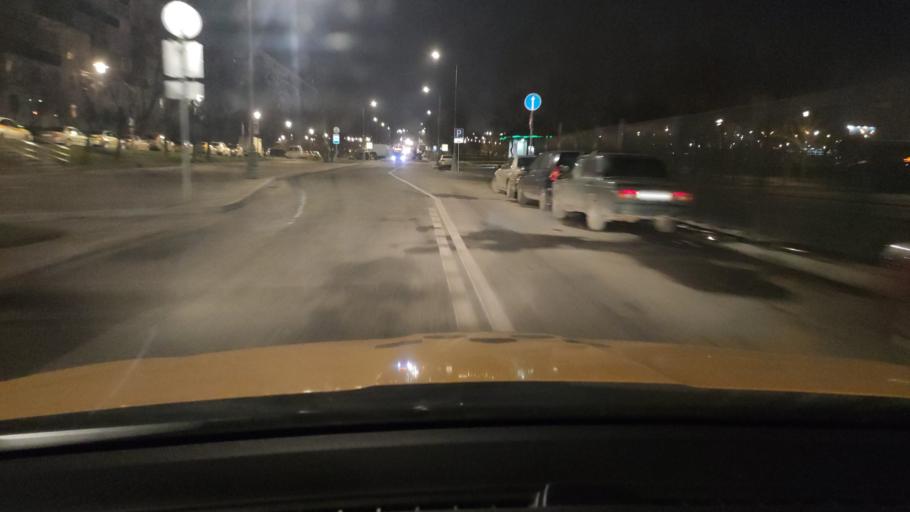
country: RU
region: Moskovskaya
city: Alekseyevka
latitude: 55.6288
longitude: 37.7980
